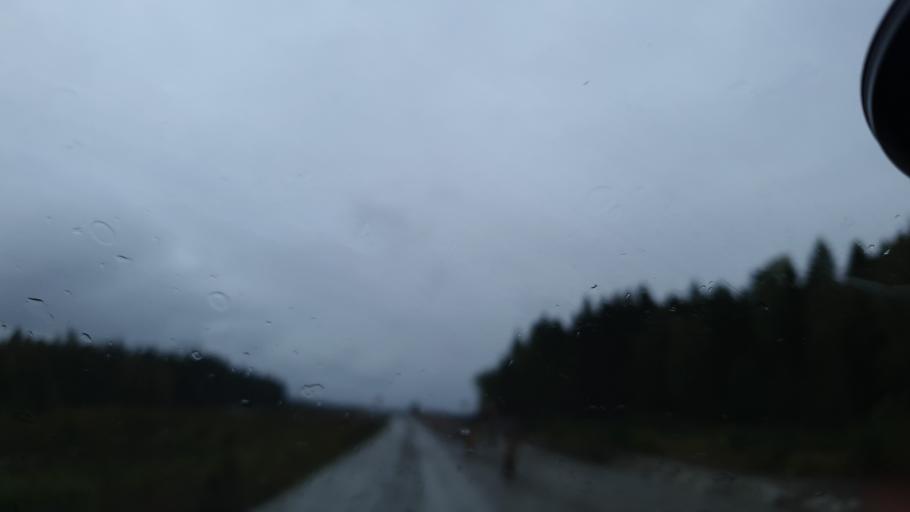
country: SE
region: Vaesterbotten
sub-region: Skelleftea Kommun
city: Soedra Bergsbyn
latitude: 64.7419
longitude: 21.0706
